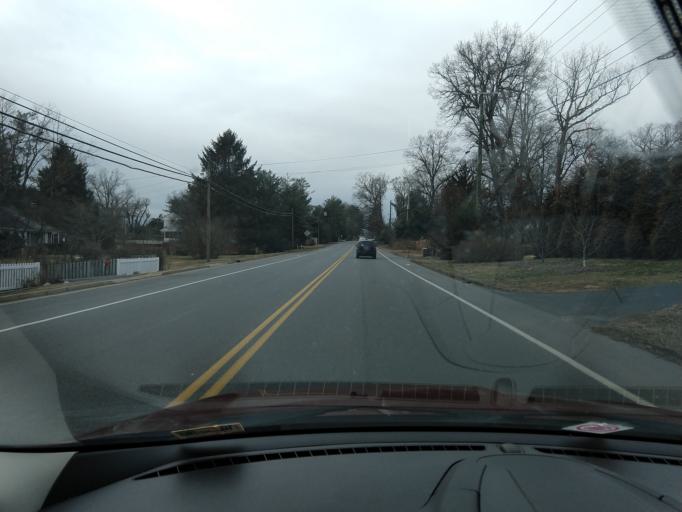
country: US
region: Virginia
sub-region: City of Waynesboro
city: Waynesboro
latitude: 38.0697
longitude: -78.9142
